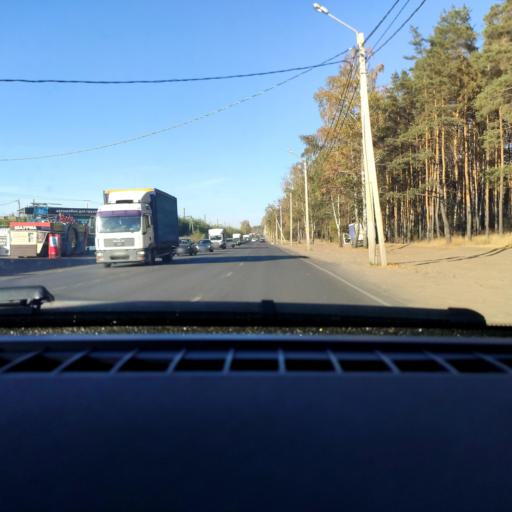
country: RU
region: Voronezj
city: Voronezh
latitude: 51.6726
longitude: 39.2723
